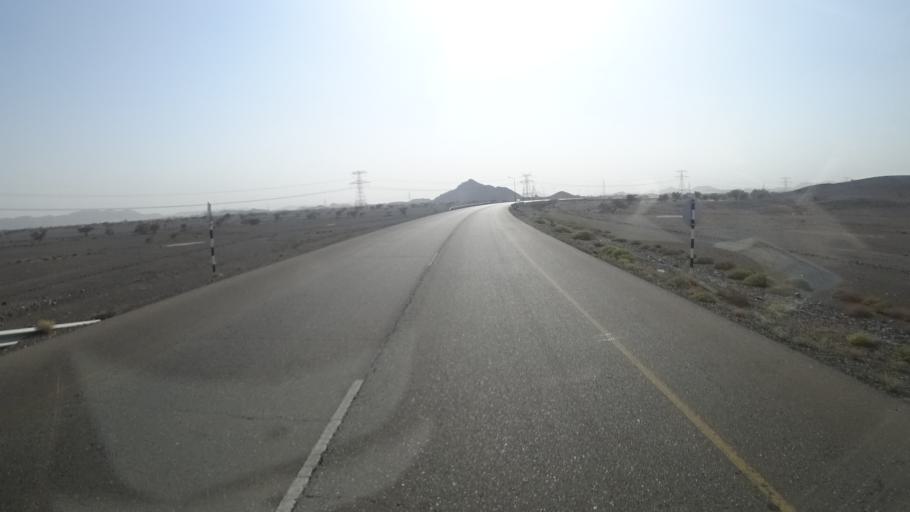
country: OM
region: Muhafazat ad Dakhiliyah
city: Izki
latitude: 22.7957
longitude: 57.8719
